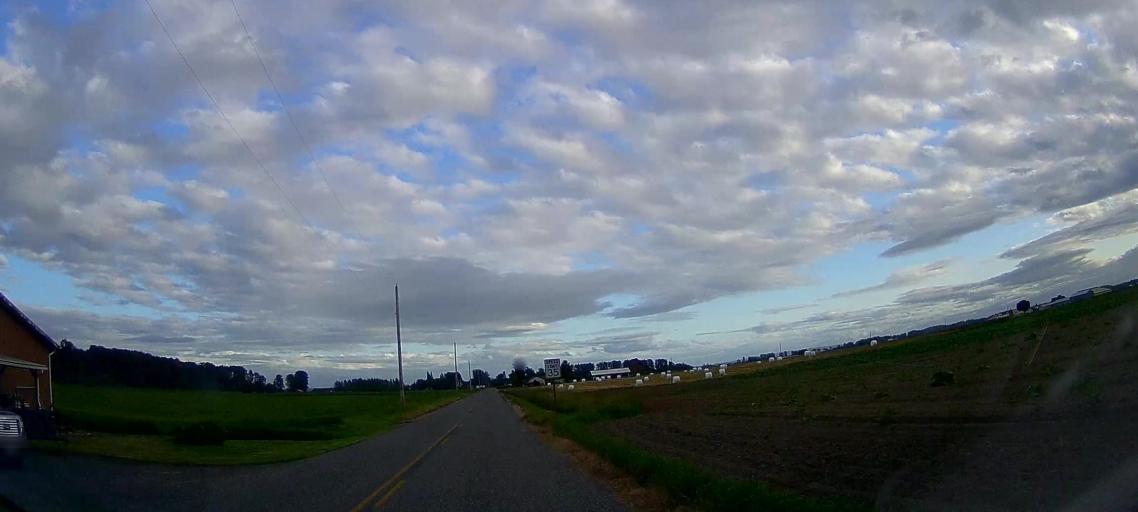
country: US
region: Washington
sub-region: Skagit County
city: Mount Vernon
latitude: 48.3983
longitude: -122.3845
